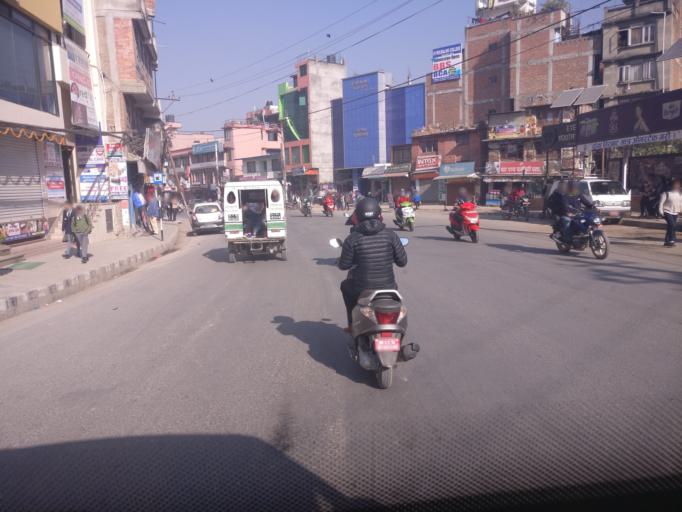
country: NP
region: Central Region
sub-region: Bagmati Zone
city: Patan
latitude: 27.6695
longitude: 85.3219
